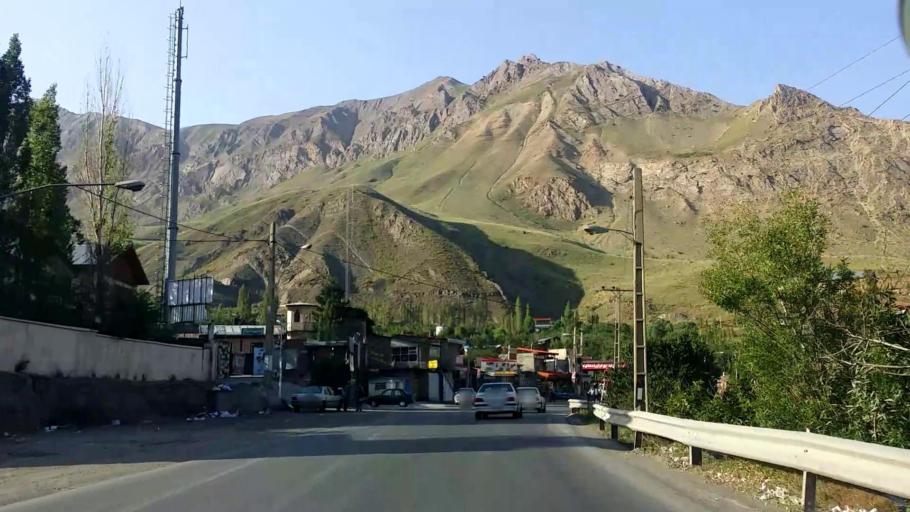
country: IR
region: Tehran
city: Tajrish
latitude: 36.0792
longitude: 51.3186
